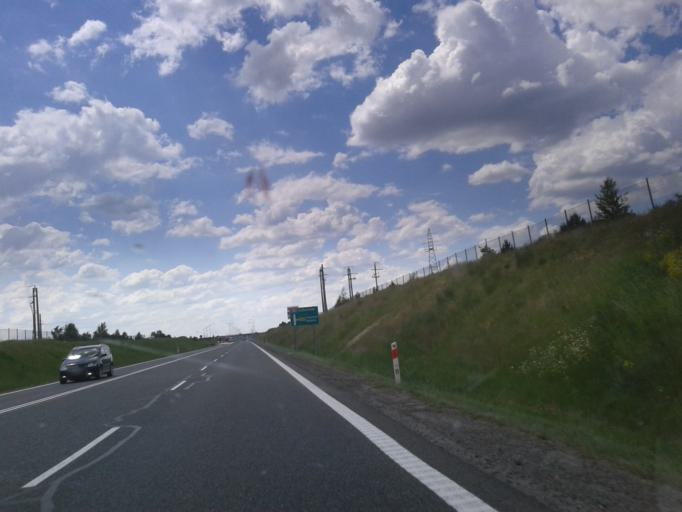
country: PL
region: Pomeranian Voivodeship
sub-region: Powiat chojnicki
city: Chojnice
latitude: 53.6968
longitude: 17.6278
